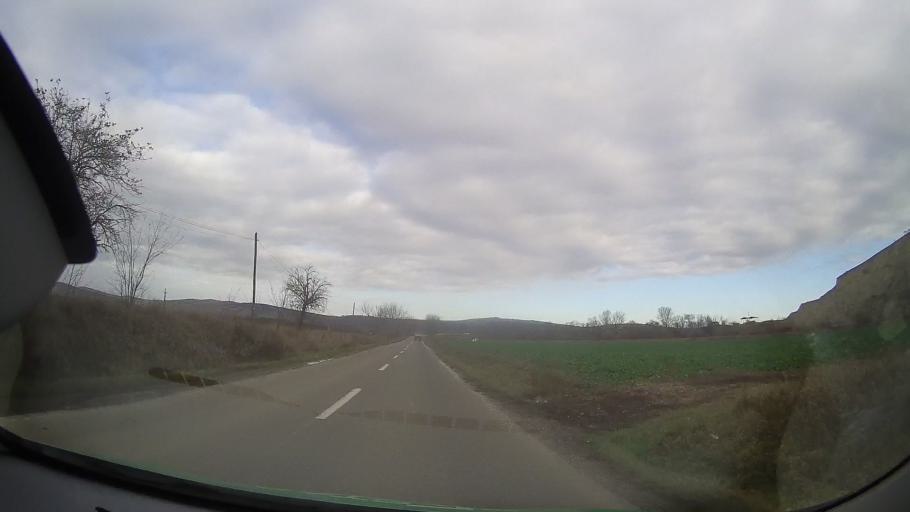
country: RO
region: Mures
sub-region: Comuna Iernut
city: Iernut
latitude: 46.4661
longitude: 24.2183
